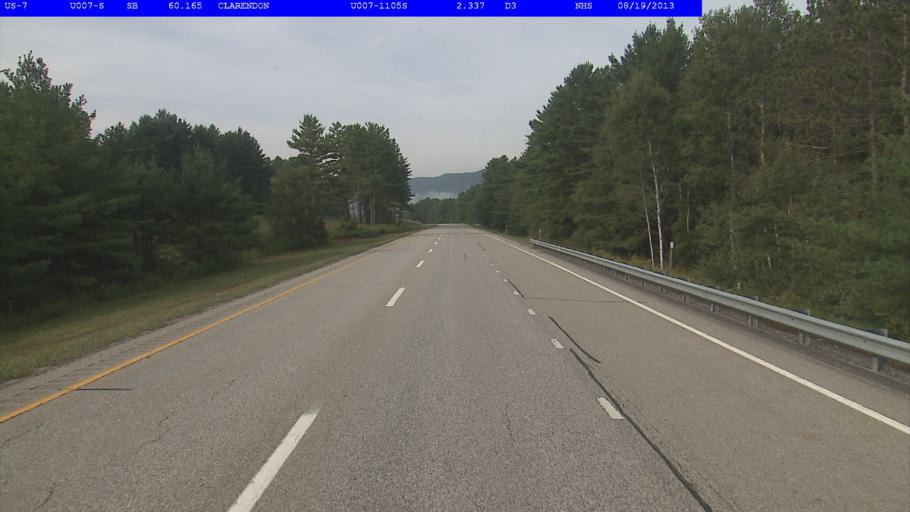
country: US
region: Vermont
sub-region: Rutland County
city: Rutland
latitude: 43.5277
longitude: -72.9633
